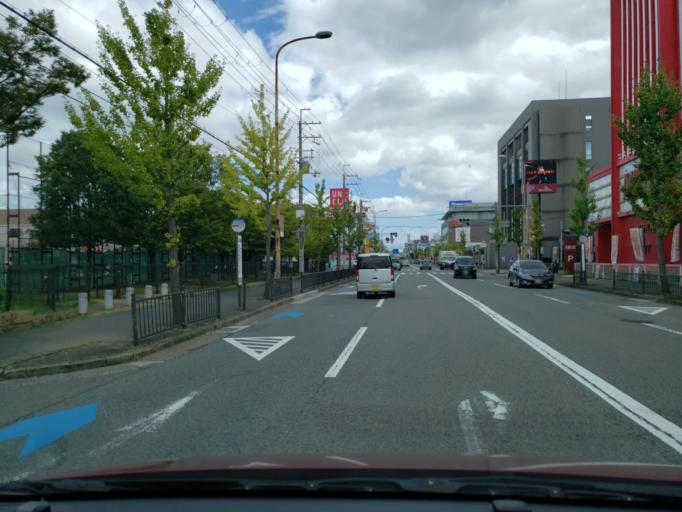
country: JP
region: Osaka
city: Toyonaka
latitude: 34.7578
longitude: 135.4669
